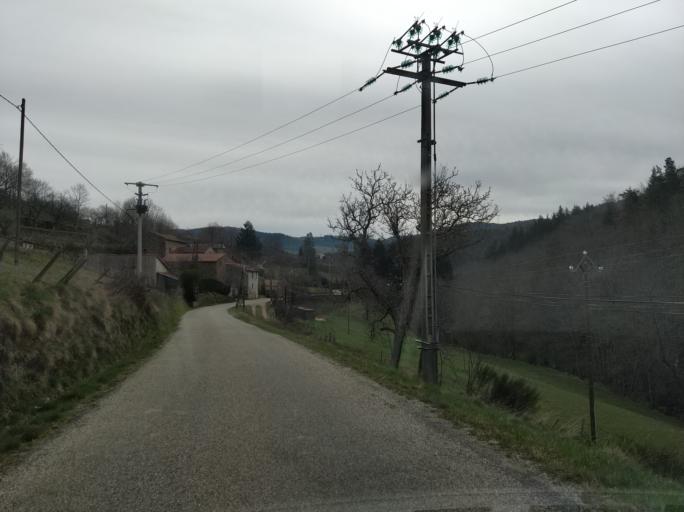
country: FR
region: Rhone-Alpes
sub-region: Departement de l'Ardeche
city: Satillieu
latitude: 45.1581
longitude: 4.5938
